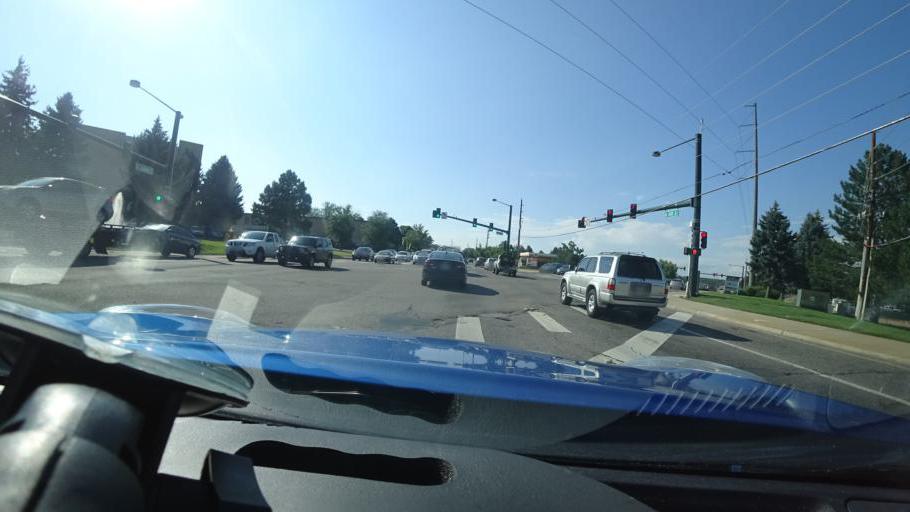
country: US
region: Colorado
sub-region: Arapahoe County
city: Glendale
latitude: 39.6765
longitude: -104.9034
